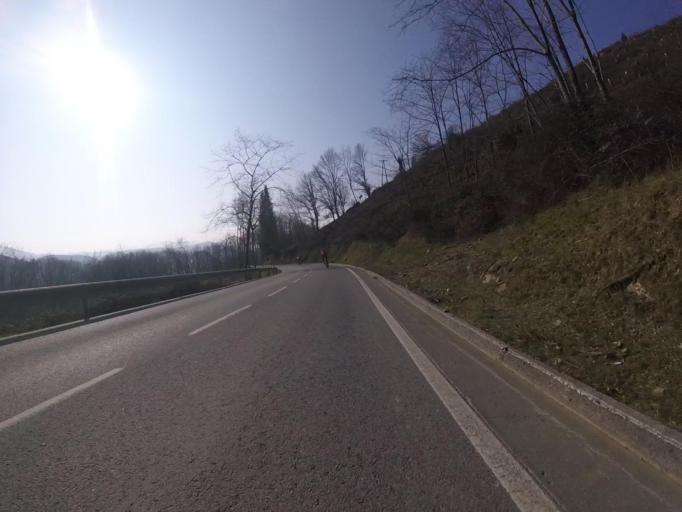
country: ES
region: Navarre
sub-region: Provincia de Navarra
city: Bera
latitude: 43.3026
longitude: -1.6895
